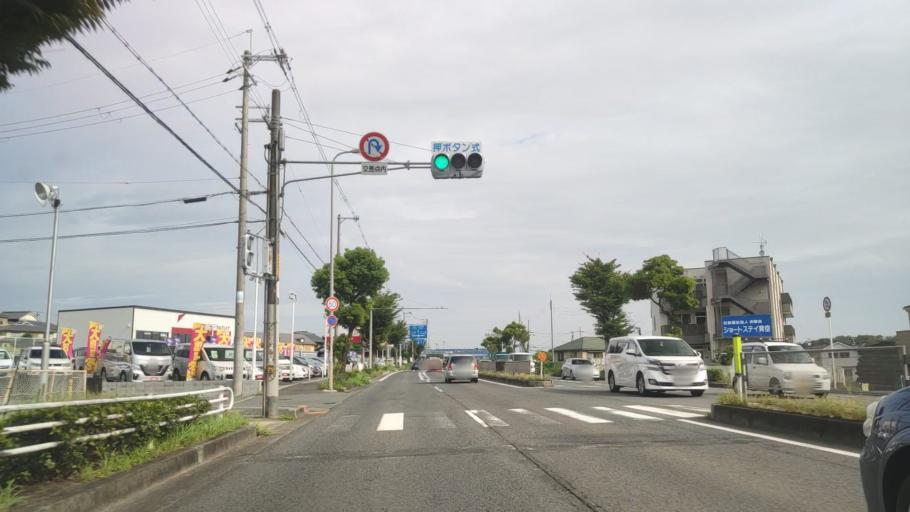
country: JP
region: Osaka
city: Tondabayashicho
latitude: 34.4663
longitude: 135.5751
